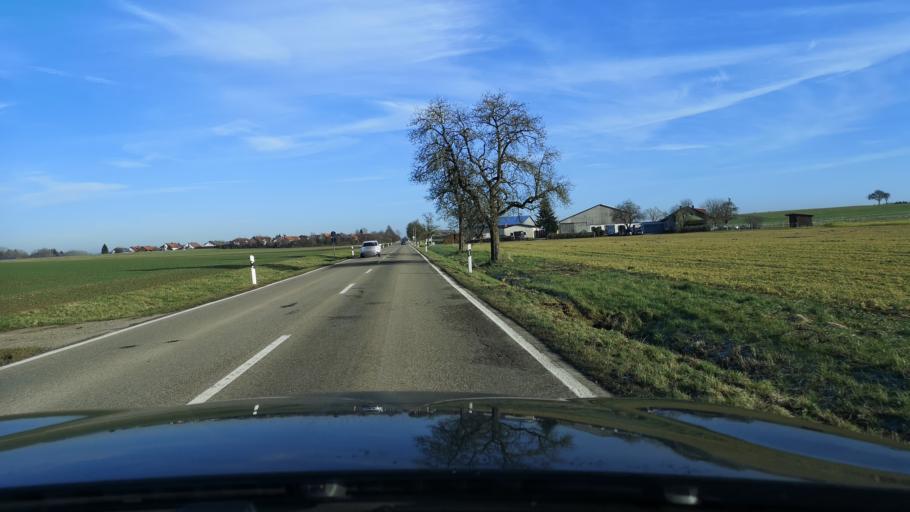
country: DE
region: Baden-Wuerttemberg
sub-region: Regierungsbezirk Stuttgart
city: Obergroningen
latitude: 48.8916
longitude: 9.8964
